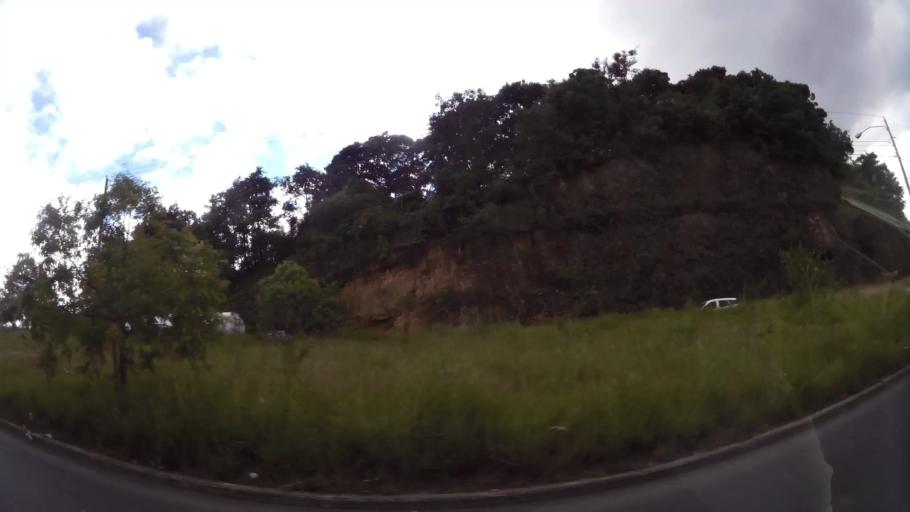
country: GT
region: Guatemala
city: Guatemala City
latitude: 14.6616
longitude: -90.5536
